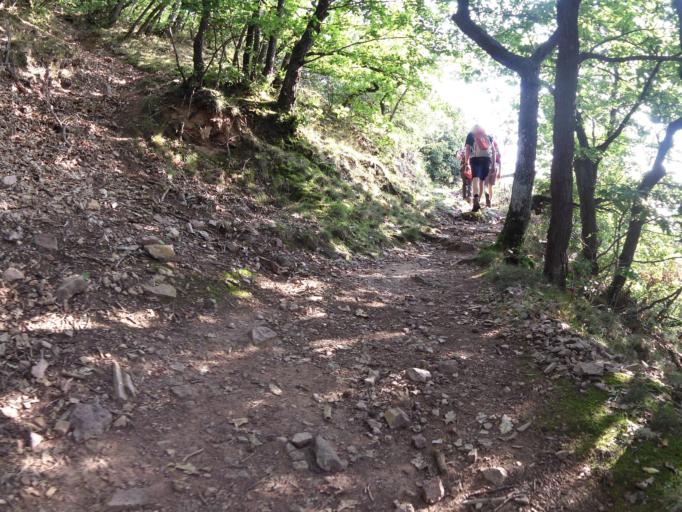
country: DE
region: Rheinland-Pfalz
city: Bad Munster am Stein-Ebernburg
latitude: 49.8168
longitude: 7.8420
